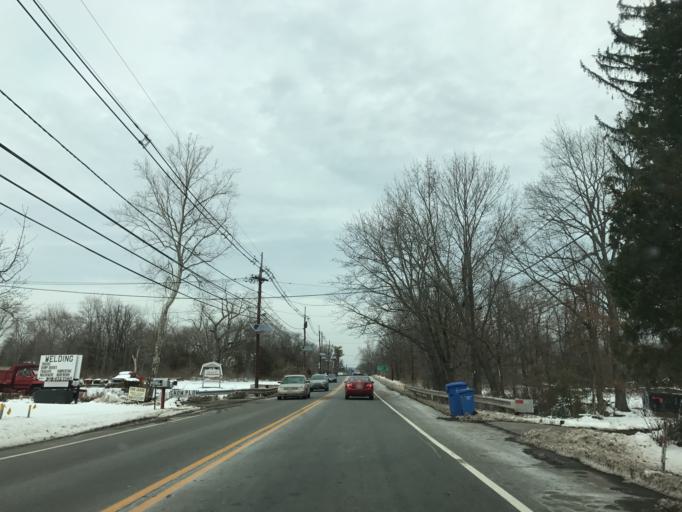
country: US
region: New Jersey
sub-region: Somerset County
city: Weston
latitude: 40.5306
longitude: -74.6240
